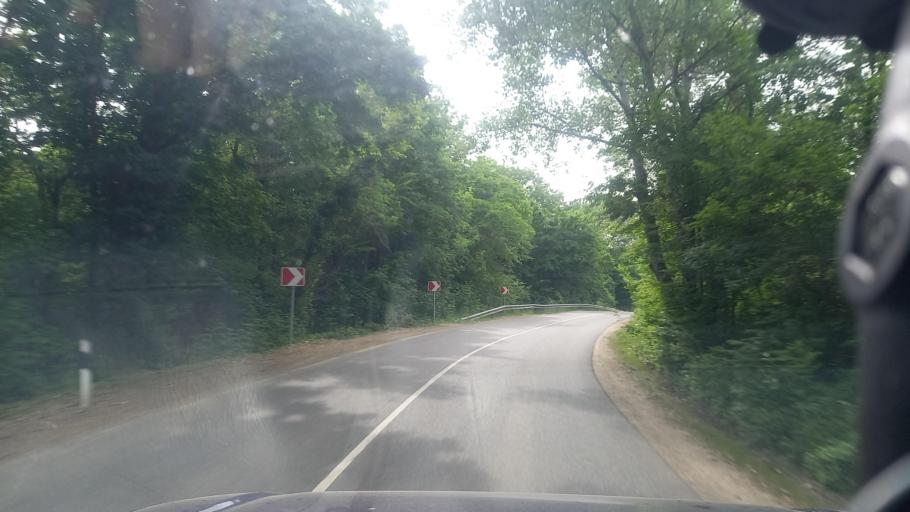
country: RU
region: Krasnodarskiy
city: Goryachiy Klyuch
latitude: 44.6018
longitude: 39.0430
